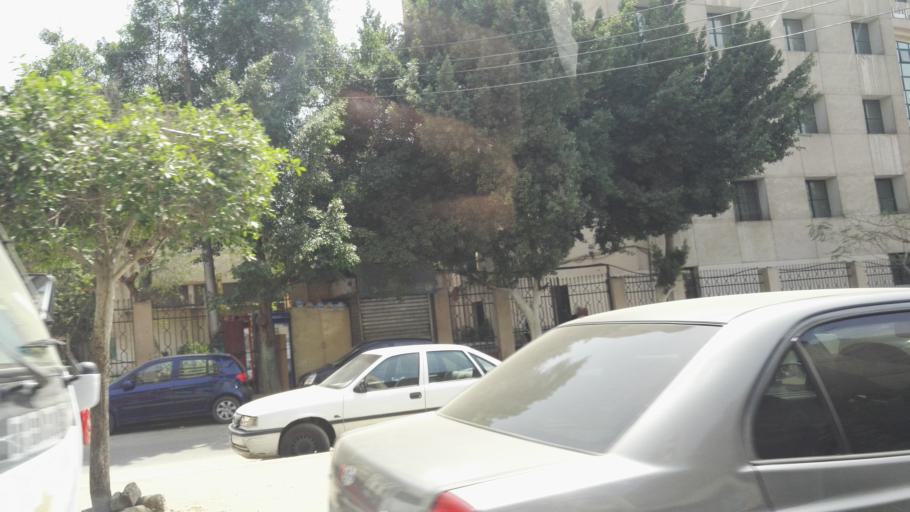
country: EG
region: Muhafazat al Qahirah
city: Cairo
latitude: 30.0813
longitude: 31.3345
